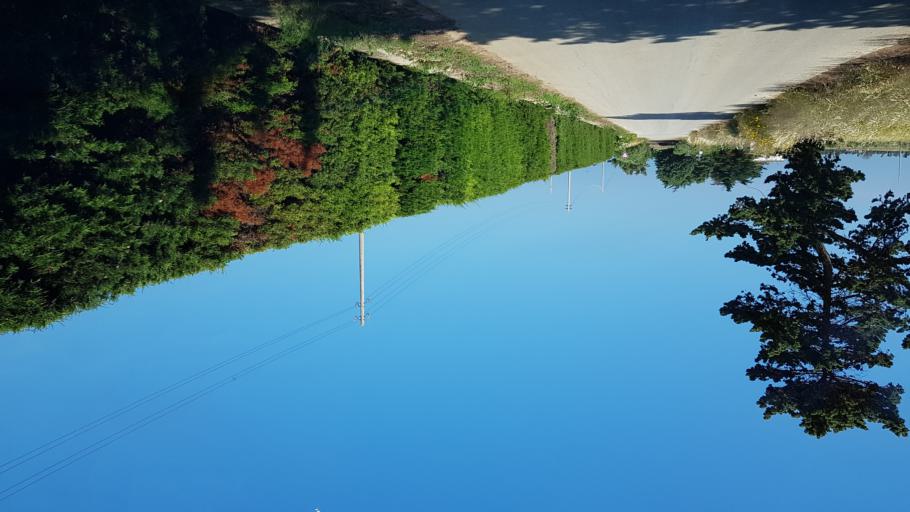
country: IT
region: Apulia
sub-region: Provincia di Brindisi
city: Brindisi
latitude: 40.6674
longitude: 17.8619
